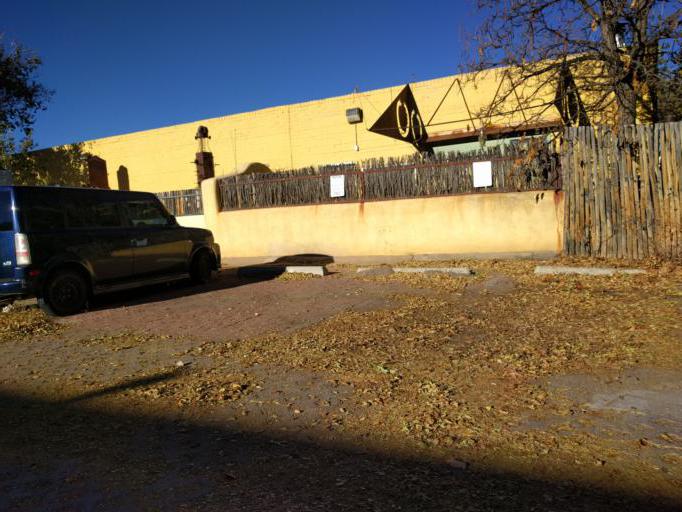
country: US
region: New Mexico
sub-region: Santa Fe County
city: Santa Fe
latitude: 35.6634
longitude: -105.9653
